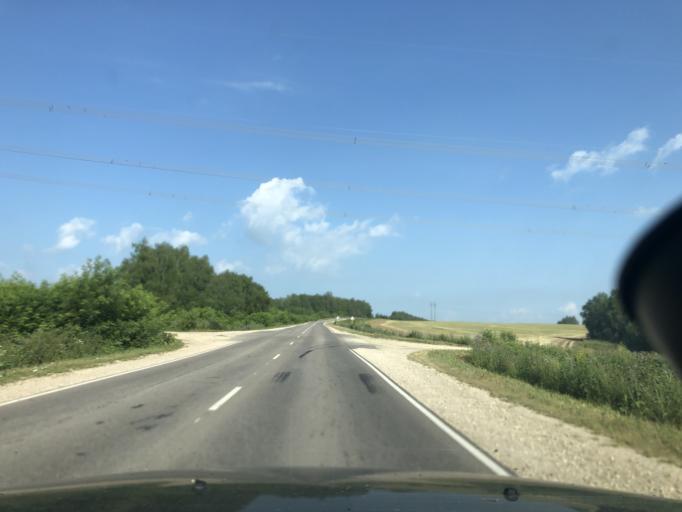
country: RU
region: Tula
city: Dubna
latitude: 54.1147
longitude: 37.0877
